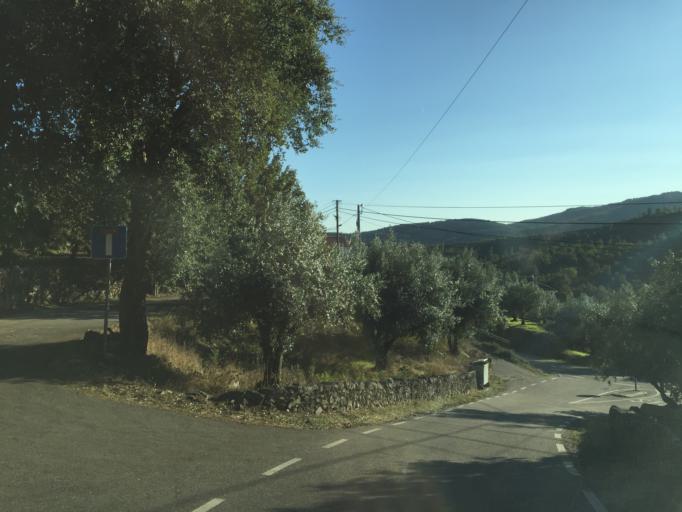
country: PT
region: Portalegre
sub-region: Marvao
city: Marvao
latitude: 39.3954
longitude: -7.3894
